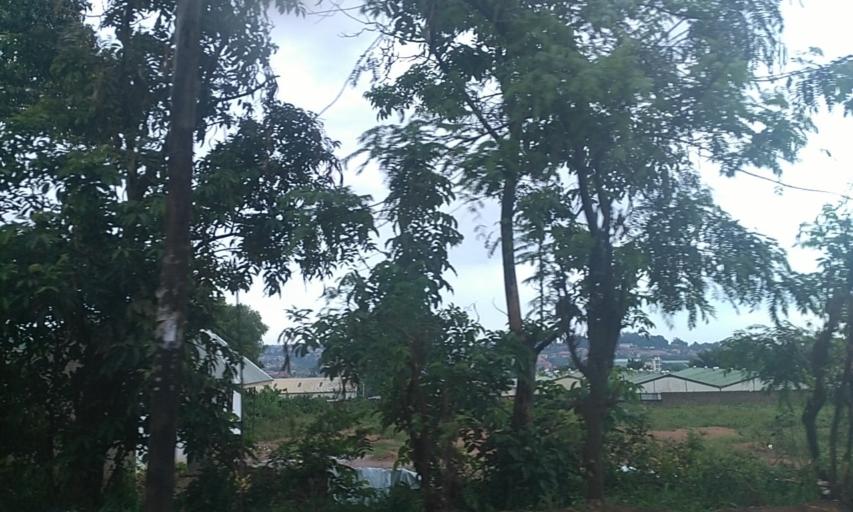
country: UG
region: Central Region
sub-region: Wakiso District
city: Bweyogerere
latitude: 0.3636
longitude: 32.6660
